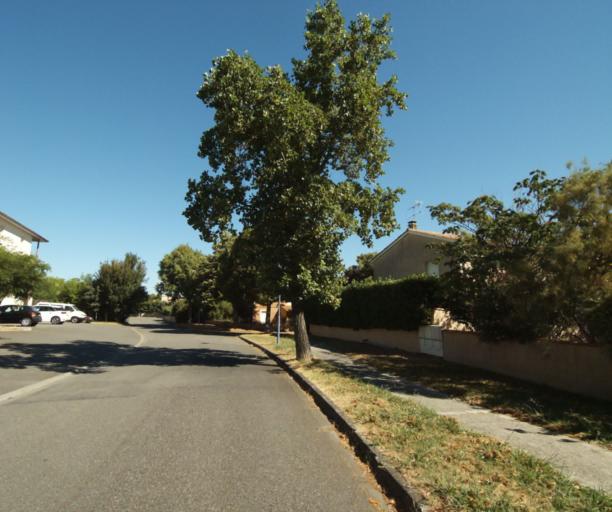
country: FR
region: Midi-Pyrenees
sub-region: Departement de la Haute-Garonne
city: Castanet-Tolosan
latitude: 43.5244
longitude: 1.4965
